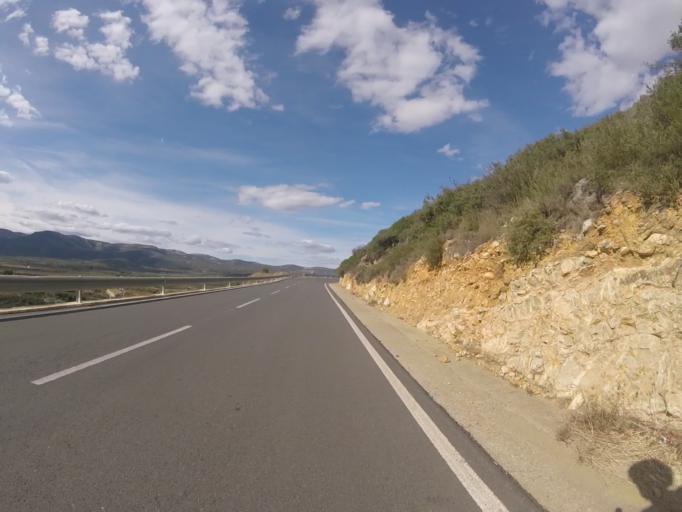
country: ES
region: Valencia
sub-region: Provincia de Castello
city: Cuevas de Vinroma
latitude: 40.3174
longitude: 0.1307
